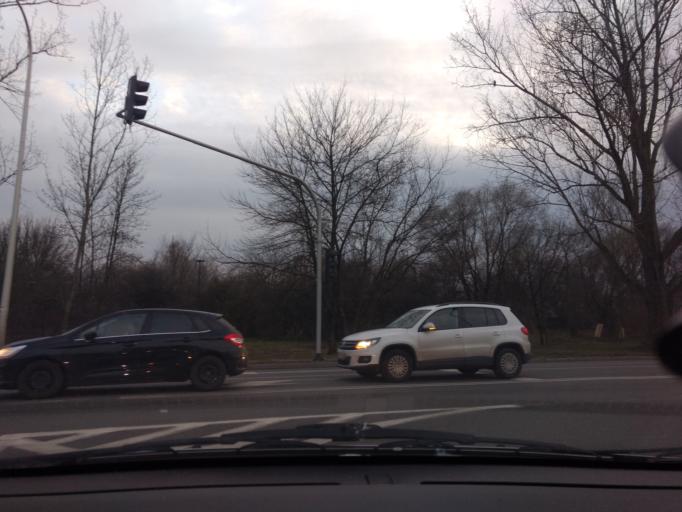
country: PL
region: Masovian Voivodeship
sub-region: Warszawa
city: Praga Poludnie
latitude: 52.2262
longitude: 21.0776
